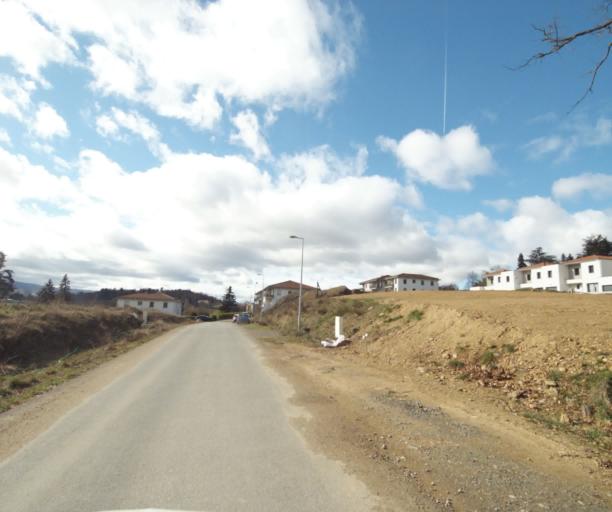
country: FR
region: Rhone-Alpes
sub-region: Departement de la Loire
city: La Talaudiere
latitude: 45.4806
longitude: 4.4218
